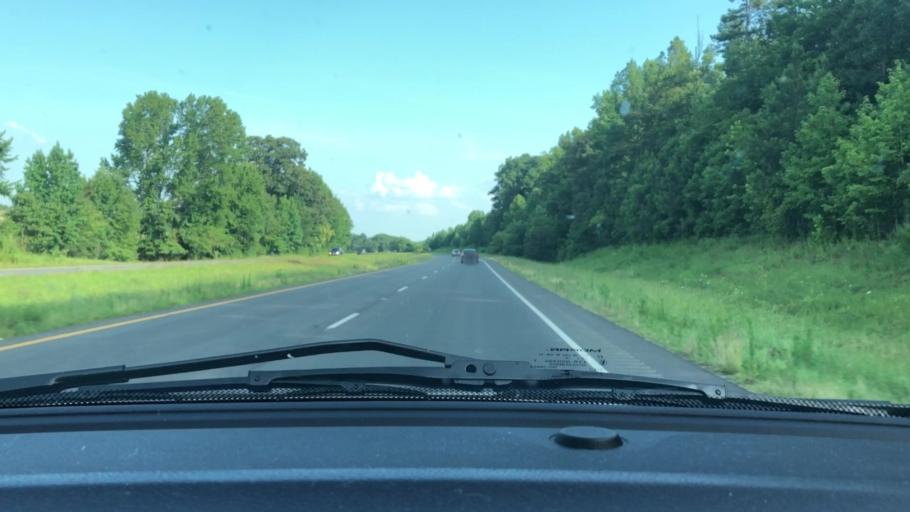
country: US
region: North Carolina
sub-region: Chatham County
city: Siler City
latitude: 35.6714
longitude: -79.4117
